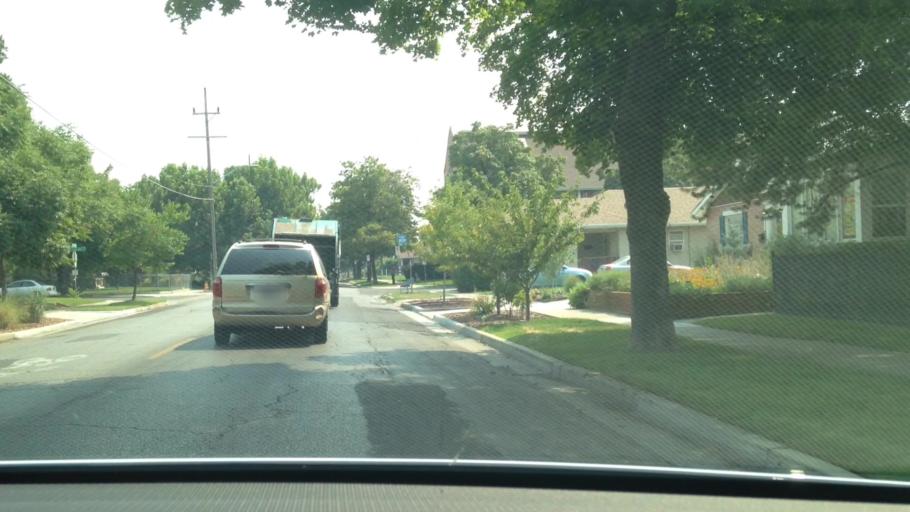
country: US
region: Utah
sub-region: Salt Lake County
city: South Salt Lake
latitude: 40.7278
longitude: -111.8769
